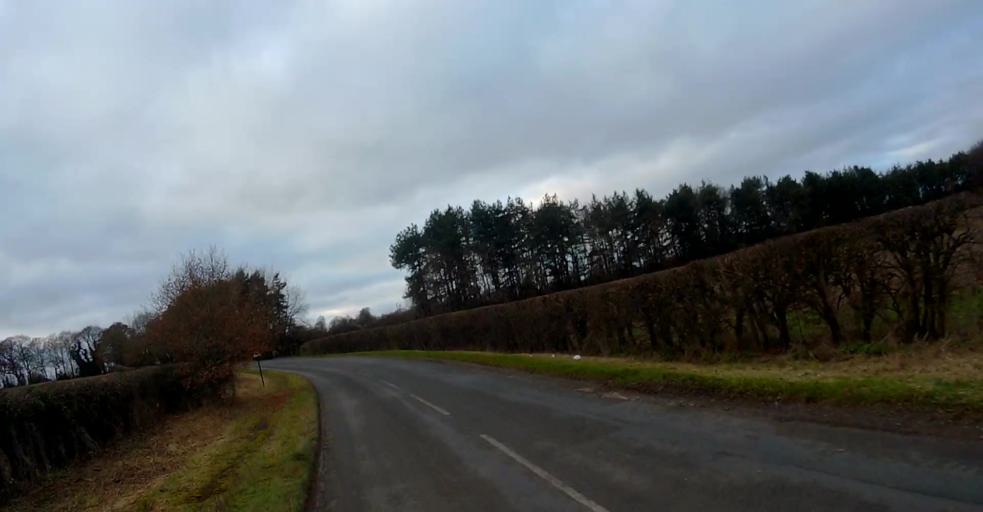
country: GB
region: England
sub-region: Hampshire
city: Overton
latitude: 51.2033
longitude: -1.1781
